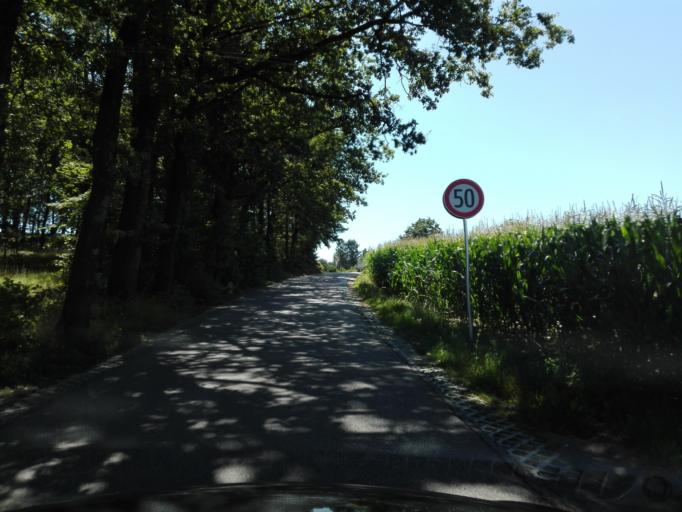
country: AT
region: Upper Austria
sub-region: Politischer Bezirk Urfahr-Umgebung
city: Engerwitzdorf
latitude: 48.3218
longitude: 14.4284
